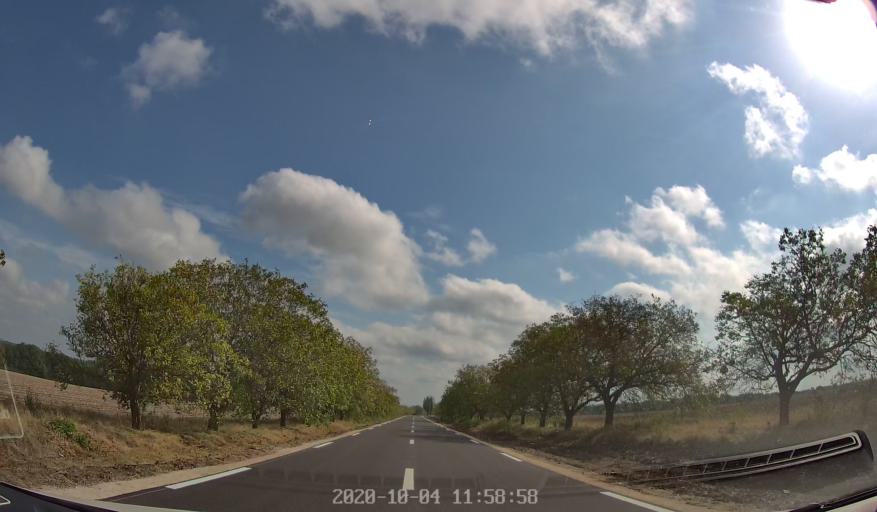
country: MD
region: Rezina
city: Saharna
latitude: 47.6334
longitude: 28.8416
